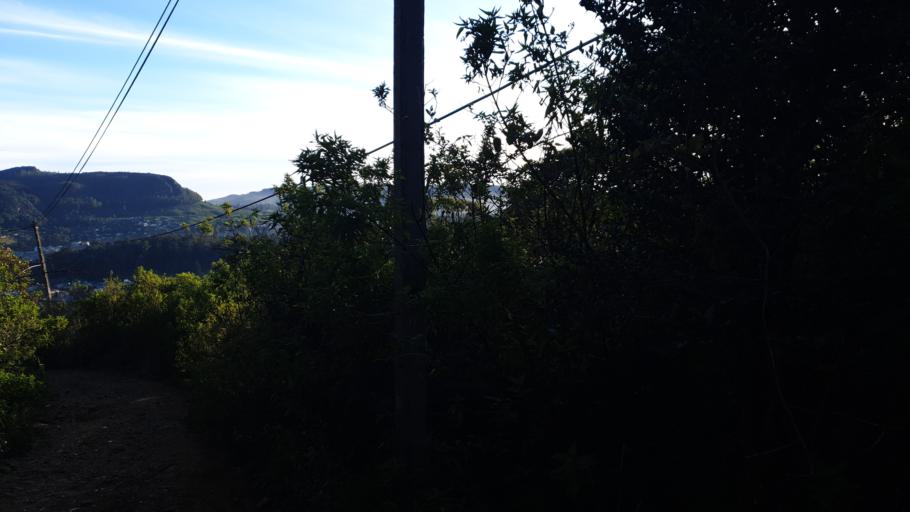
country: LK
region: Central
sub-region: Nuwara Eliya District
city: Nuwara Eliya
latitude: 6.9570
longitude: 80.7631
